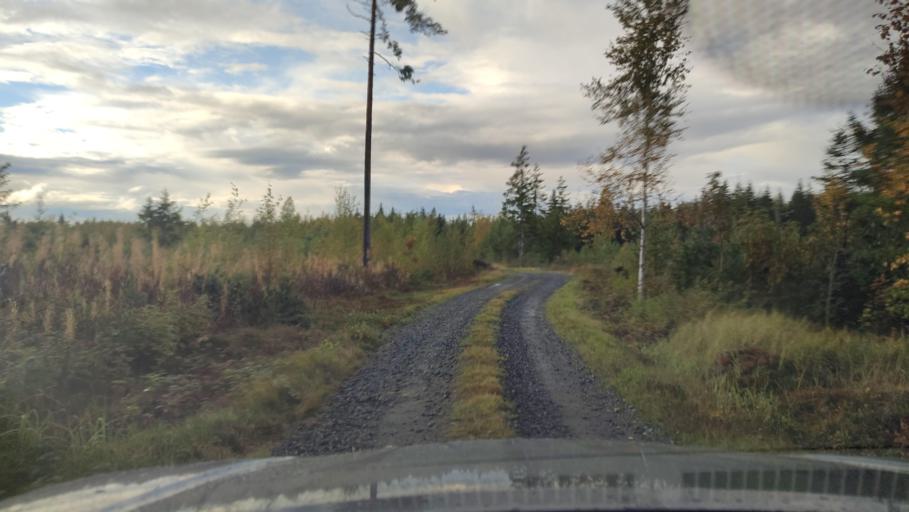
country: FI
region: Ostrobothnia
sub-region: Sydosterbotten
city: Kristinestad
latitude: 62.3027
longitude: 21.5065
